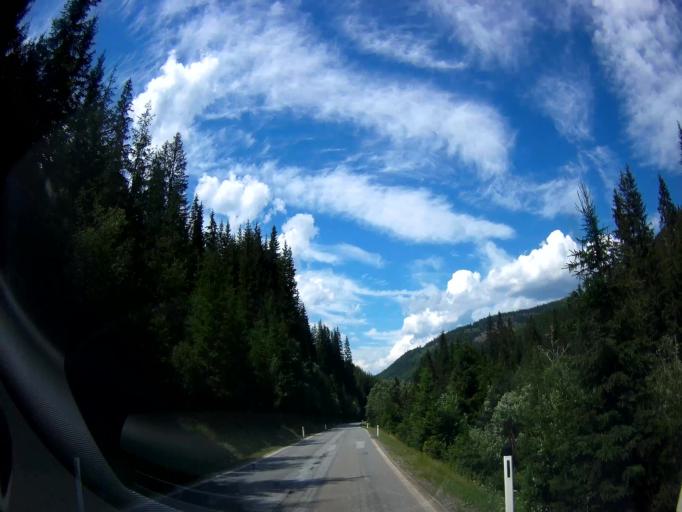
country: AT
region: Styria
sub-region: Politischer Bezirk Murau
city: Stadl an der Mur
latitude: 46.9908
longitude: 14.0149
